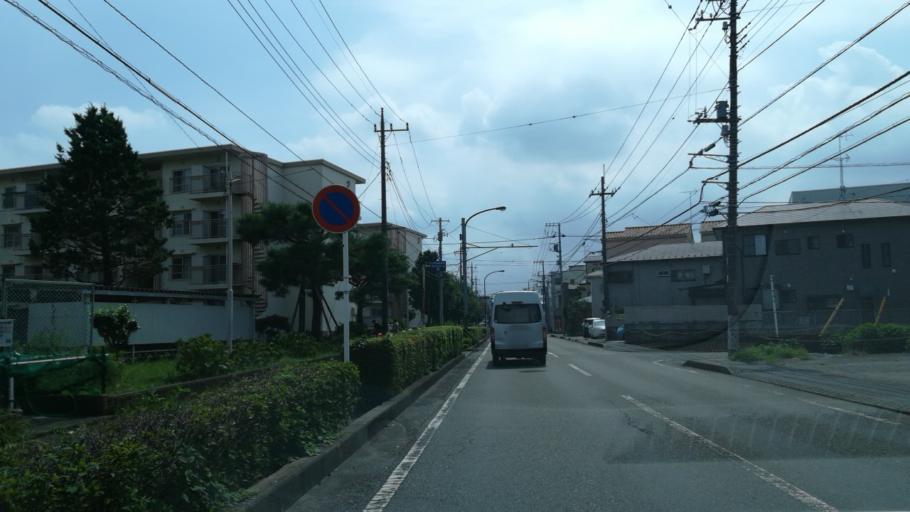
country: JP
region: Tokyo
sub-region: Machida-shi
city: Machida
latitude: 35.5636
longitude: 139.3862
